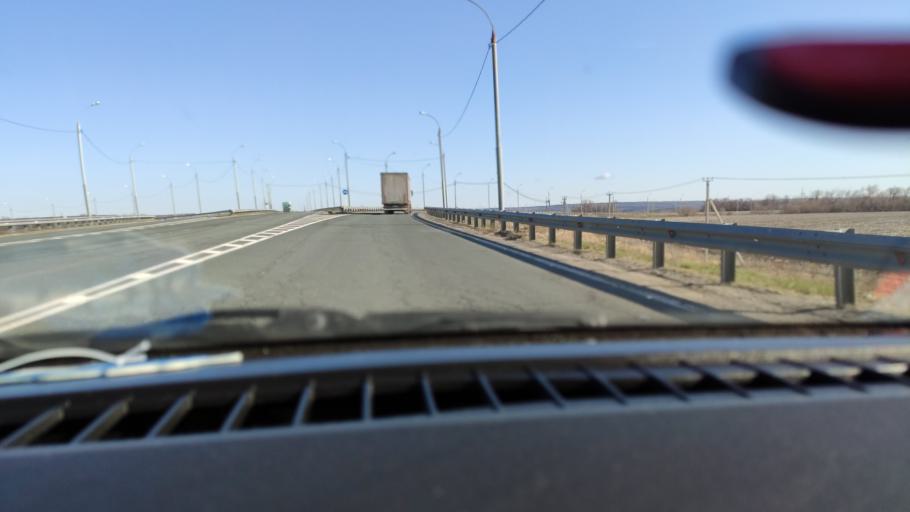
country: RU
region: Samara
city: Varlamovo
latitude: 53.1927
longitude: 48.2925
